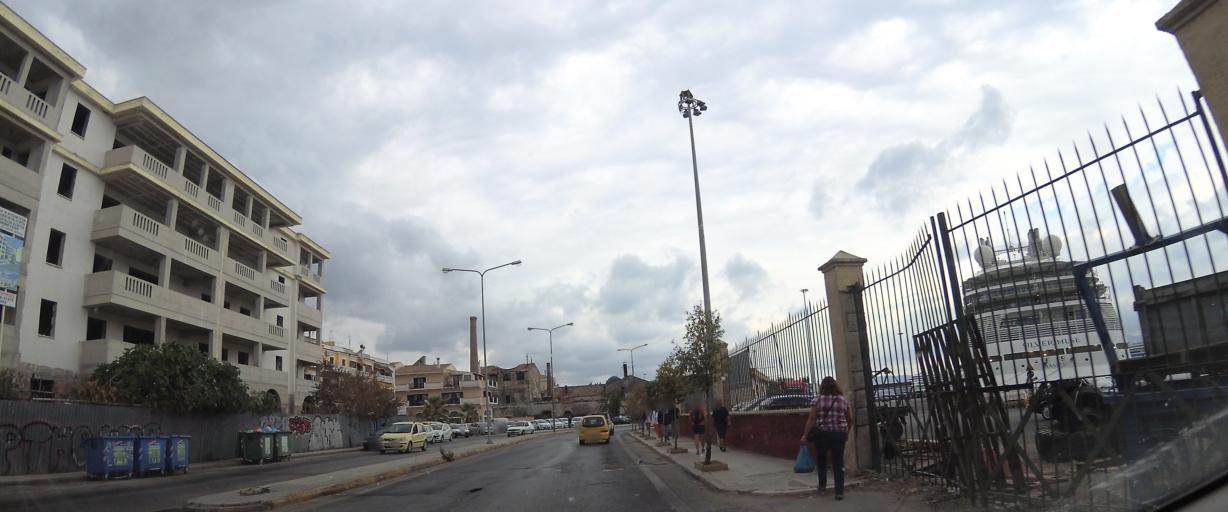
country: GR
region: Ionian Islands
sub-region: Nomos Kerkyras
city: Kerkyra
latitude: 39.6260
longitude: 19.9079
